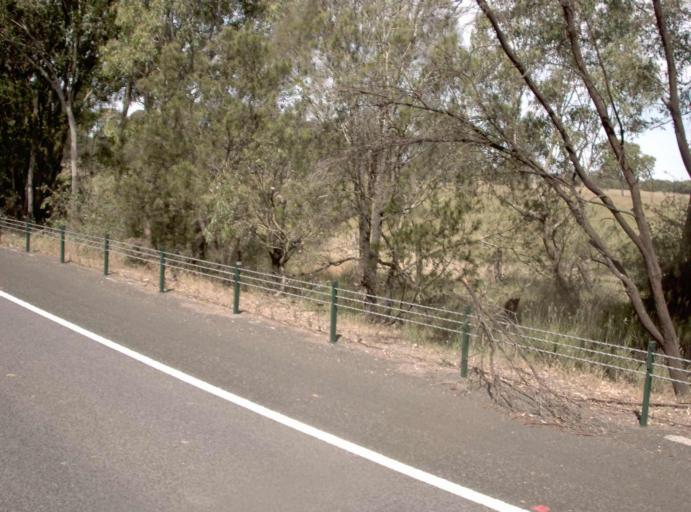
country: AU
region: Victoria
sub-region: Wellington
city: Sale
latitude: -37.9553
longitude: 147.1015
